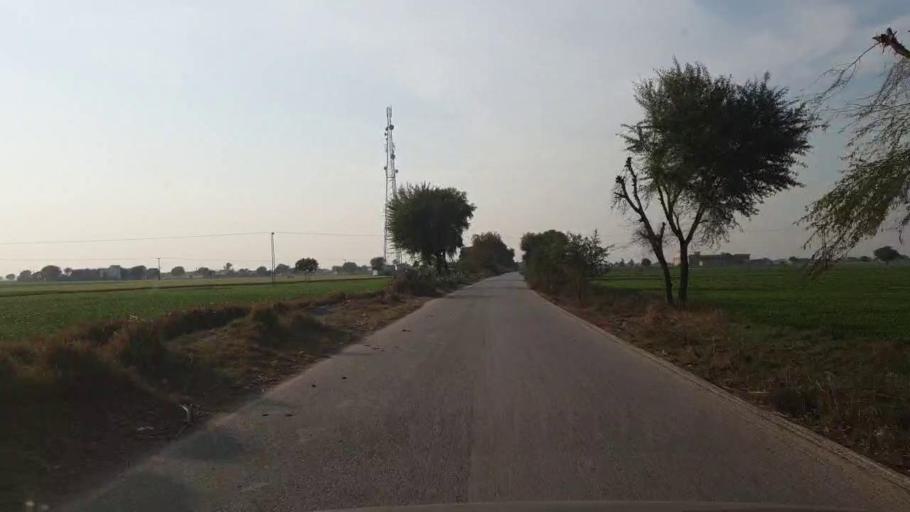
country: PK
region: Sindh
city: Shahpur Chakar
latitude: 26.1607
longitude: 68.6355
